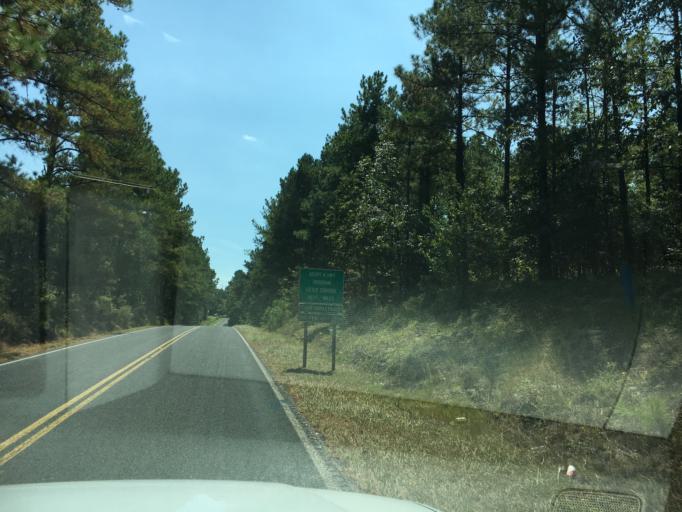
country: US
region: South Carolina
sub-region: Lexington County
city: Batesburg
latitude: 33.8145
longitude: -81.6518
